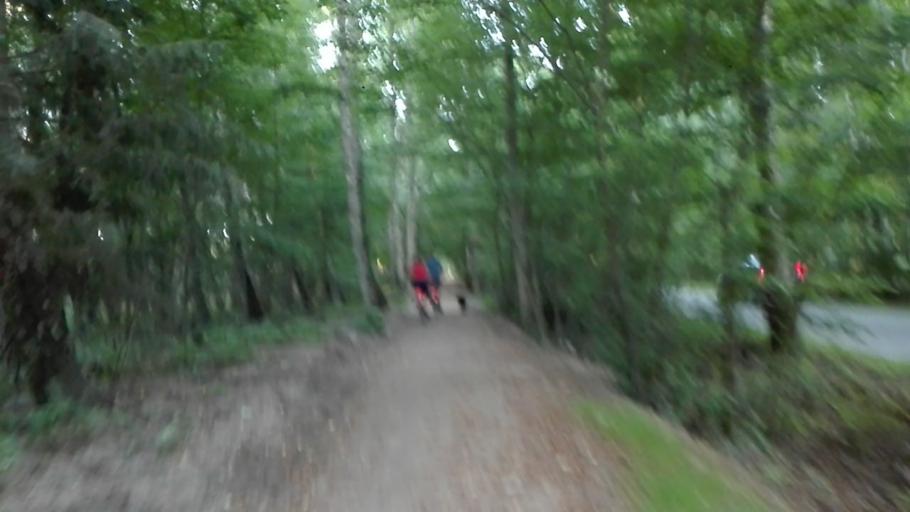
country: PL
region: West Pomeranian Voivodeship
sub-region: Powiat policki
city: Dobra
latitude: 53.4711
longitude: 14.3628
